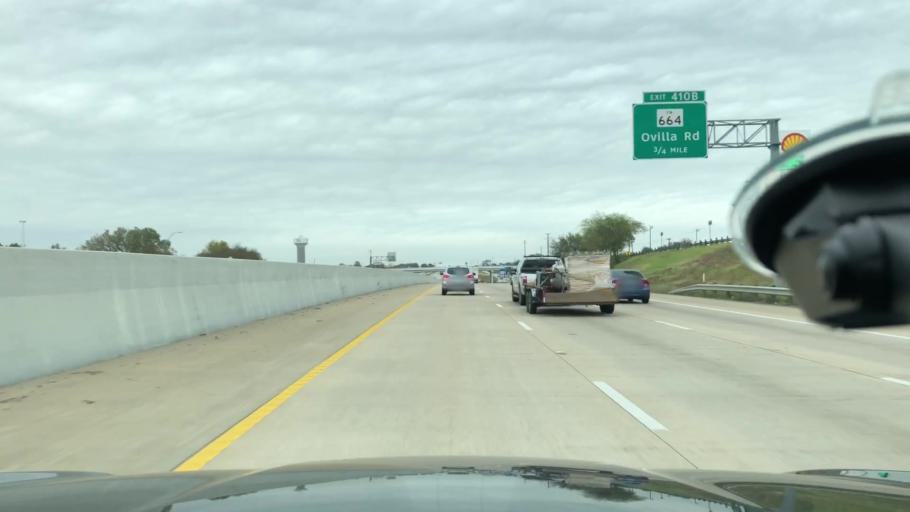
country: US
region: Texas
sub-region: Ellis County
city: Red Oak
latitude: 32.5151
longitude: -96.8221
